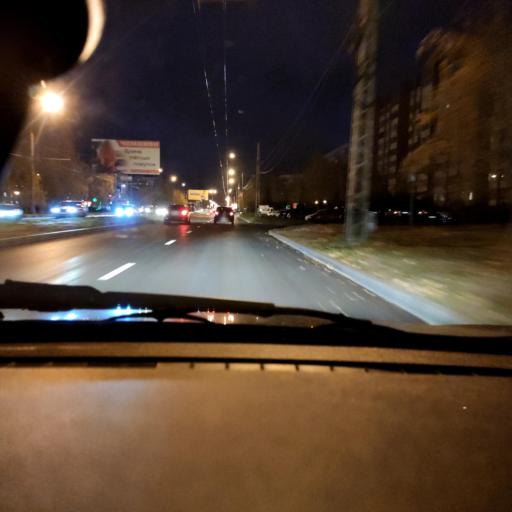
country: RU
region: Samara
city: Tol'yatti
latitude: 53.5306
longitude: 49.3280
